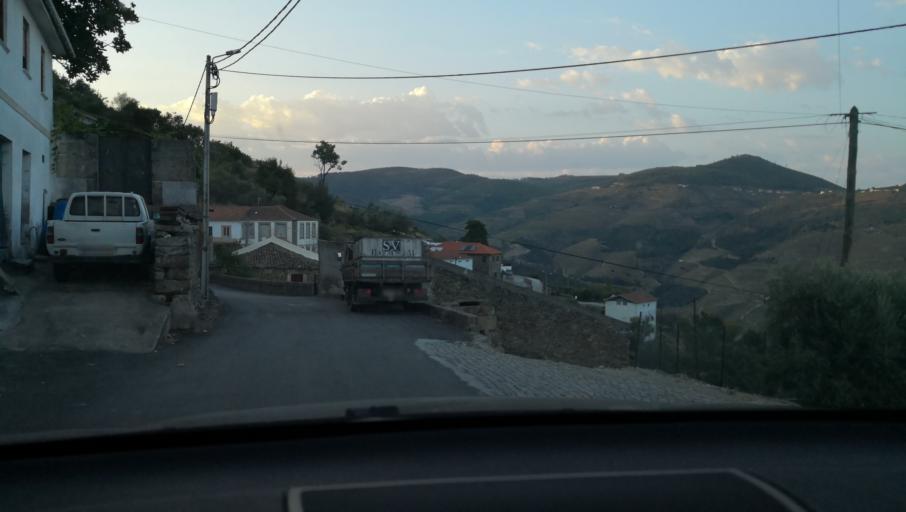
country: PT
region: Vila Real
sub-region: Sabrosa
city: Vilela
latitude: 41.1972
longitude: -7.5735
